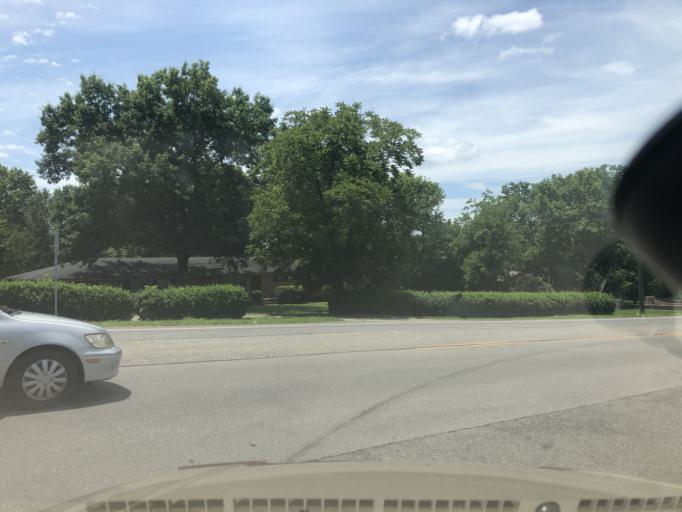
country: US
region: Tennessee
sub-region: Davidson County
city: Lakewood
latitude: 36.2493
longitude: -86.6856
